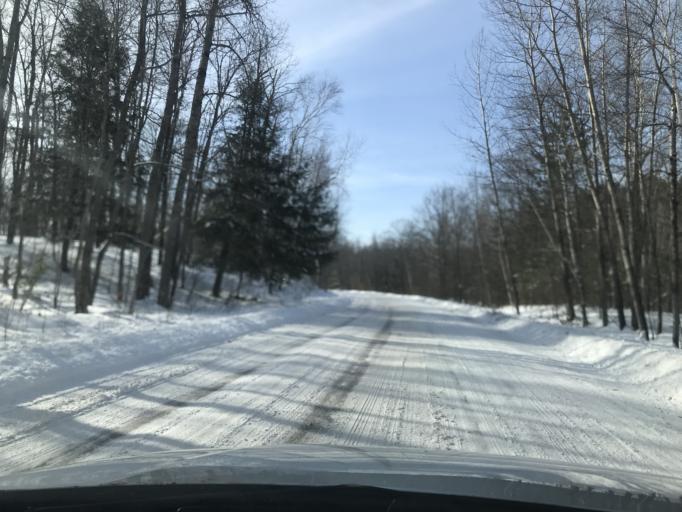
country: US
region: Wisconsin
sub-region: Oconto County
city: Gillett
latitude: 45.1573
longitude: -88.2104
